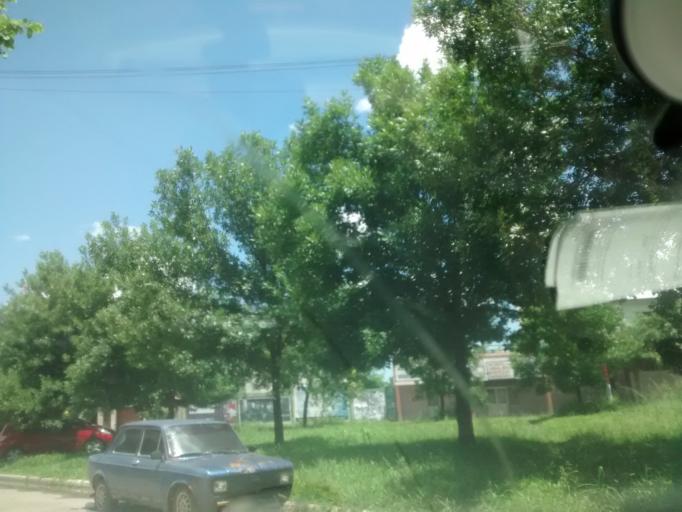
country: AR
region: Chaco
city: Resistencia
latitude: -27.4331
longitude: -58.9819
